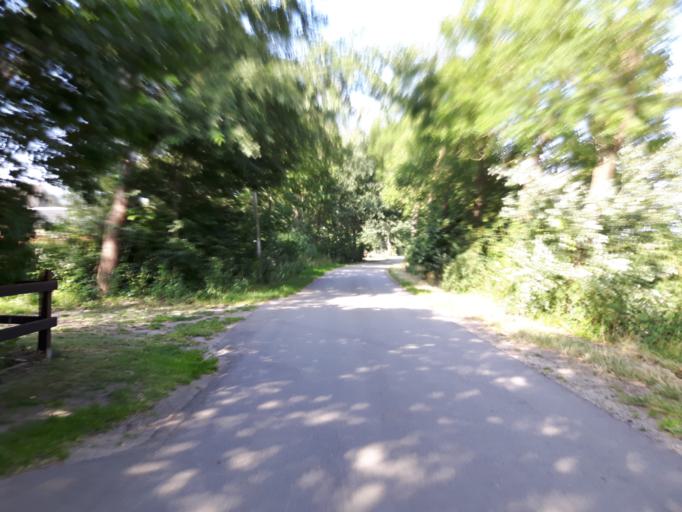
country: DE
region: Lower Saxony
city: Lemwerder
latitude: 53.1487
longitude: 8.5549
